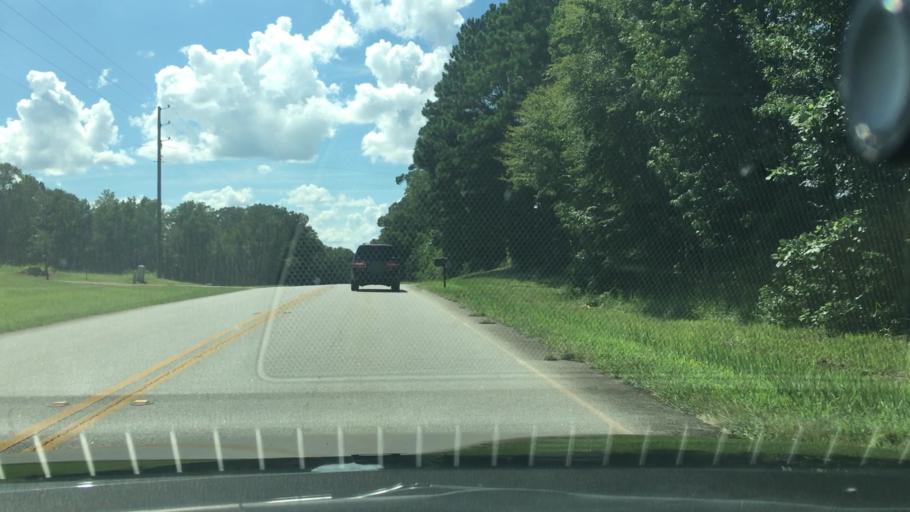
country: US
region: Georgia
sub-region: Jasper County
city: Monticello
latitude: 33.3050
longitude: -83.5842
